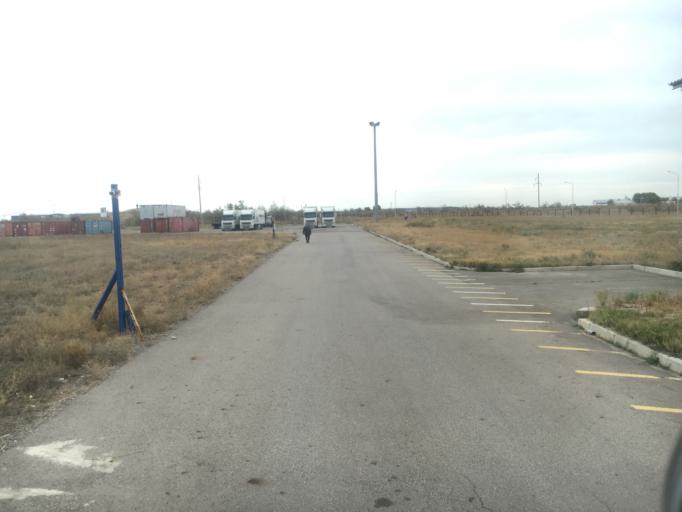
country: KZ
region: Almaty Oblysy
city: Energeticheskiy
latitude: 43.5836
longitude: 77.0976
